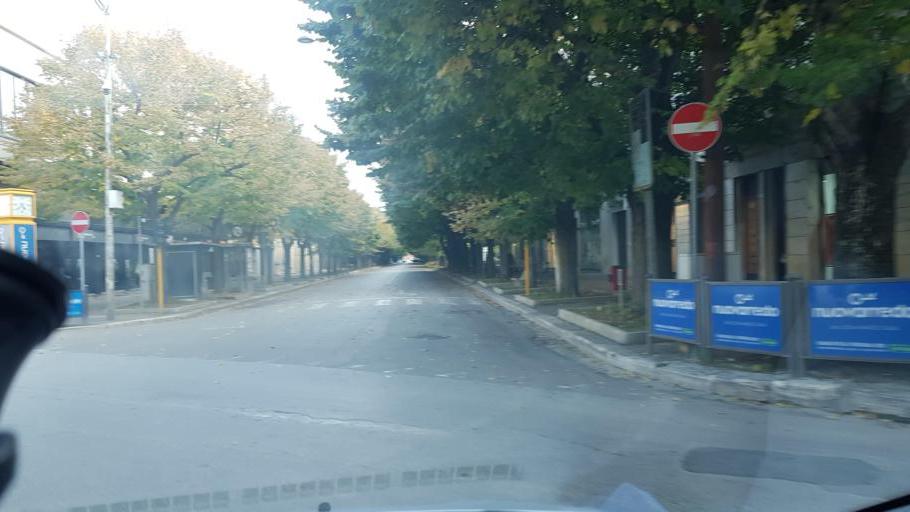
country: IT
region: Apulia
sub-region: Provincia di Brindisi
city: Francavilla Fontana
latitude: 40.5270
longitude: 17.5839
